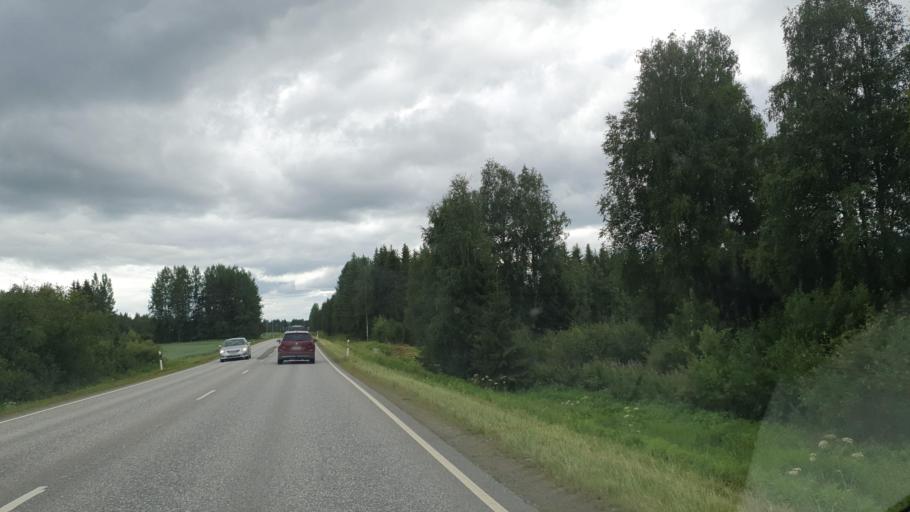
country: FI
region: Northern Savo
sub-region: Ylae-Savo
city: Sonkajaervi
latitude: 63.7350
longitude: 27.3779
